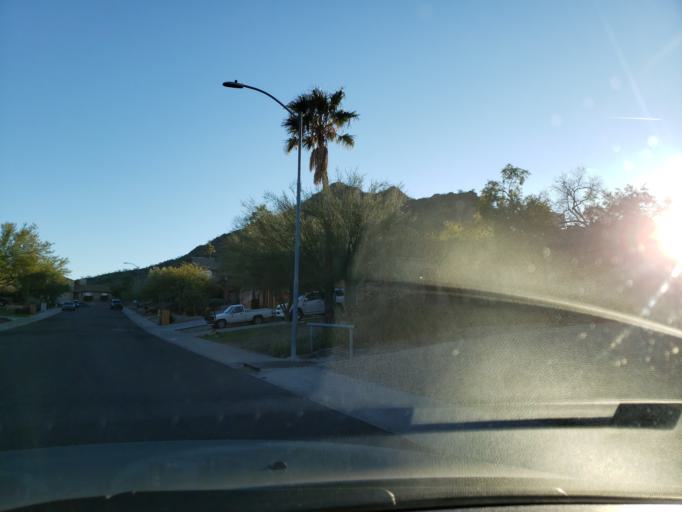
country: US
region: Arizona
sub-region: Maricopa County
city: Paradise Valley
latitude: 33.5925
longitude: -112.0344
